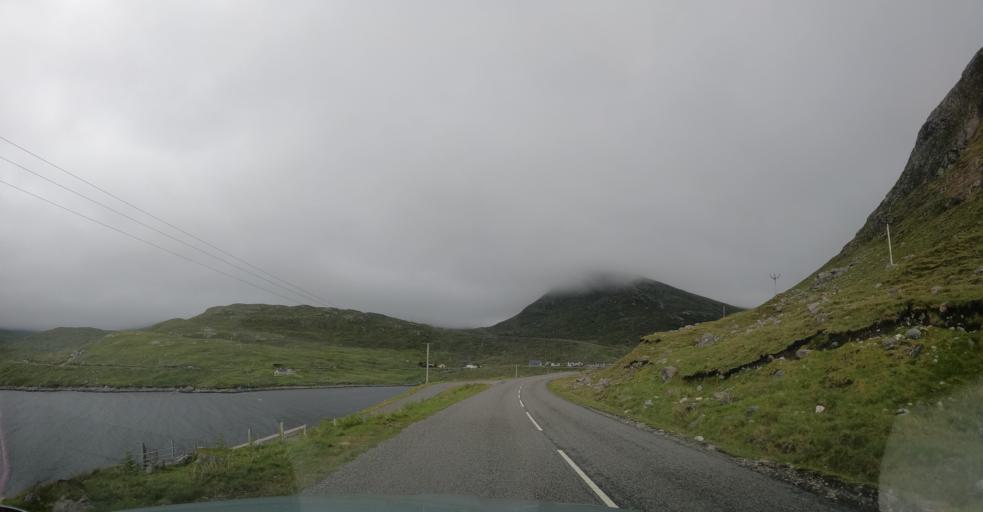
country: GB
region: Scotland
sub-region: Eilean Siar
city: Harris
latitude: 57.9258
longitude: -6.8453
